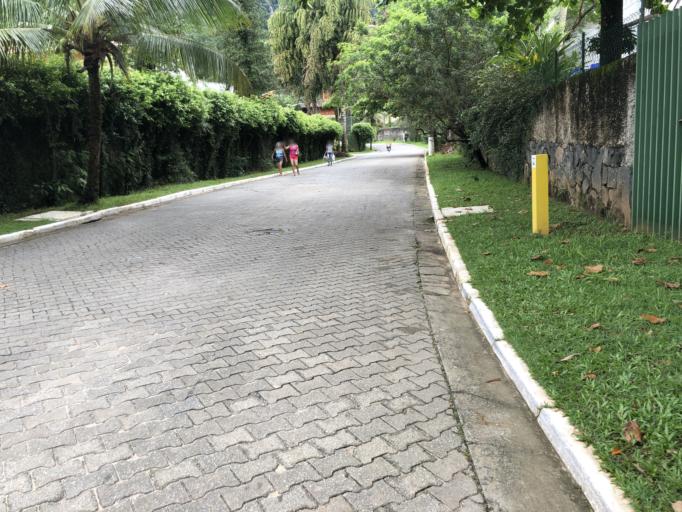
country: BR
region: Sao Paulo
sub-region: Sao Sebastiao
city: Sao Sebastiao
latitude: -23.8155
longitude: -45.5325
